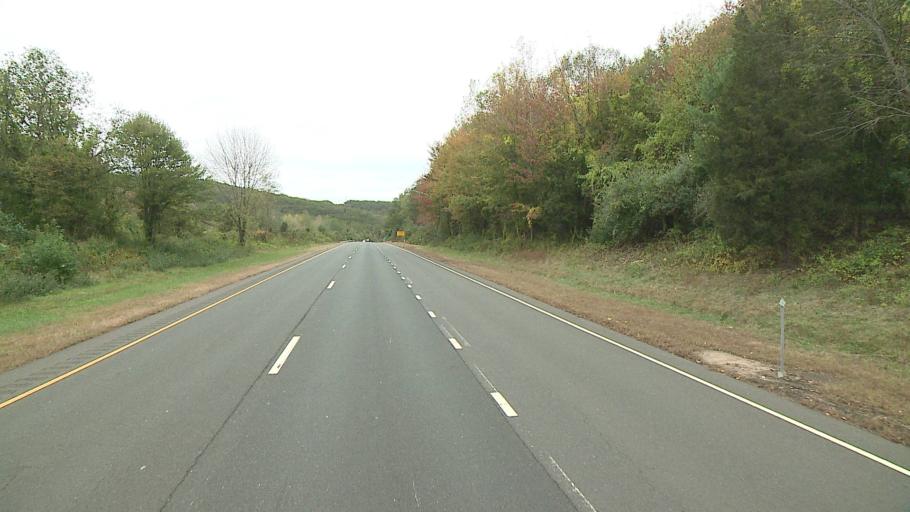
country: US
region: Connecticut
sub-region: Middlesex County
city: Higganum
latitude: 41.4687
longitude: -72.5508
